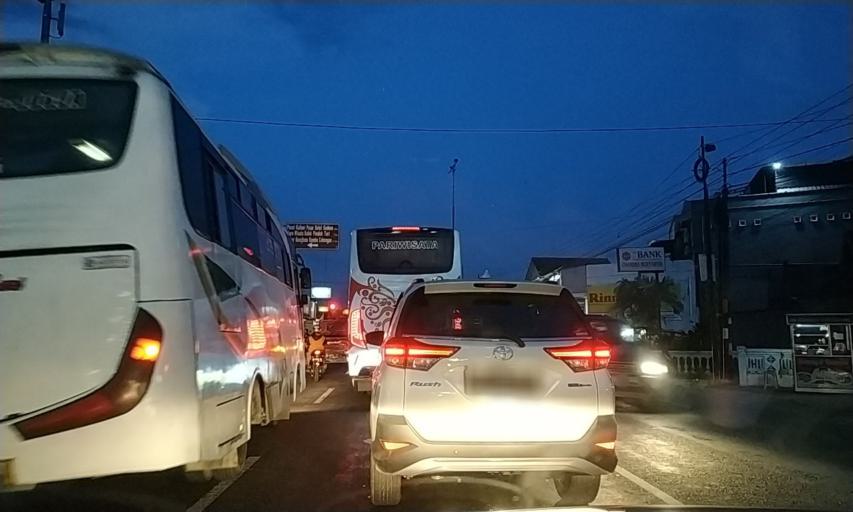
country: ID
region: Daerah Istimewa Yogyakarta
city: Godean
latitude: -7.8124
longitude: 110.2703
